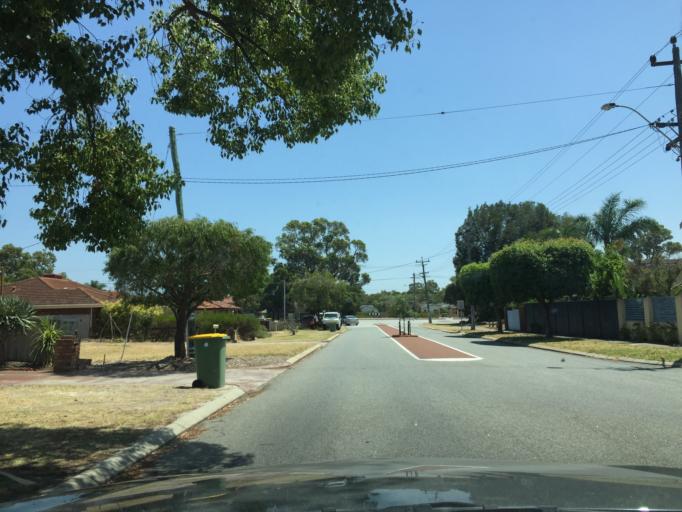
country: AU
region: Western Australia
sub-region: Canning
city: Ferndale
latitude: -32.0395
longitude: 115.9144
